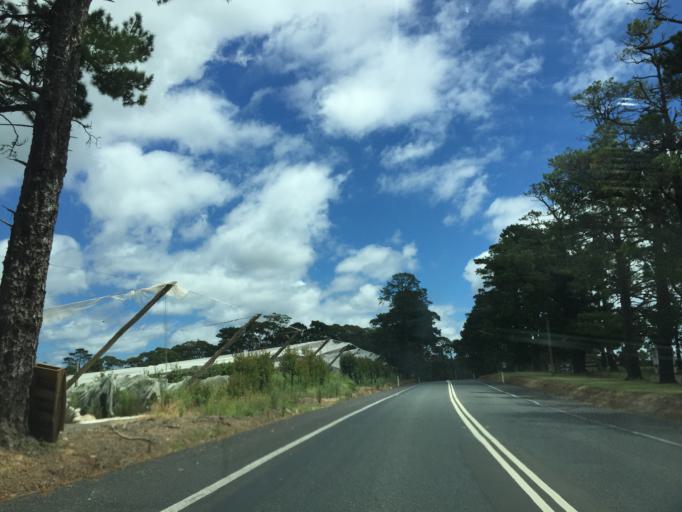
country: AU
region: New South Wales
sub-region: Hawkesbury
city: Richmond
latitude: -33.5086
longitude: 150.5570
